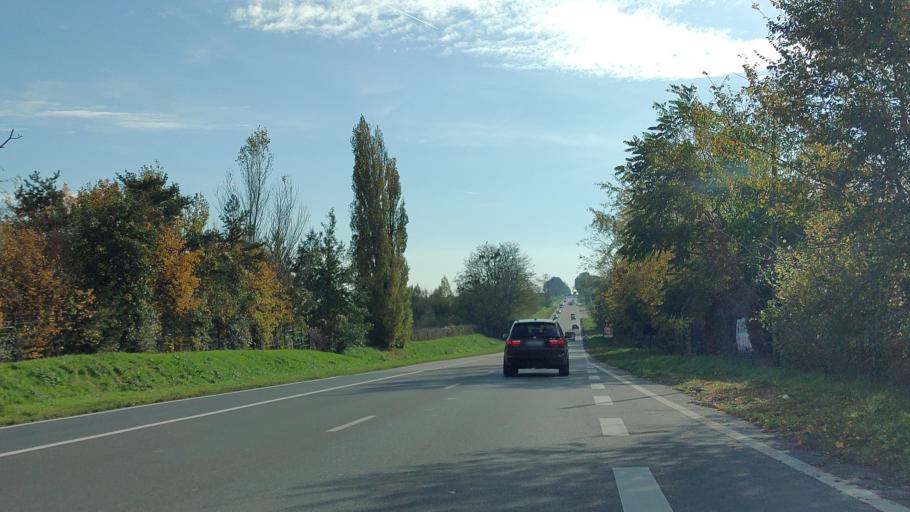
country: FR
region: Ile-de-France
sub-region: Departement du Val-d'Oise
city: Survilliers
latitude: 49.0884
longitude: 2.5298
